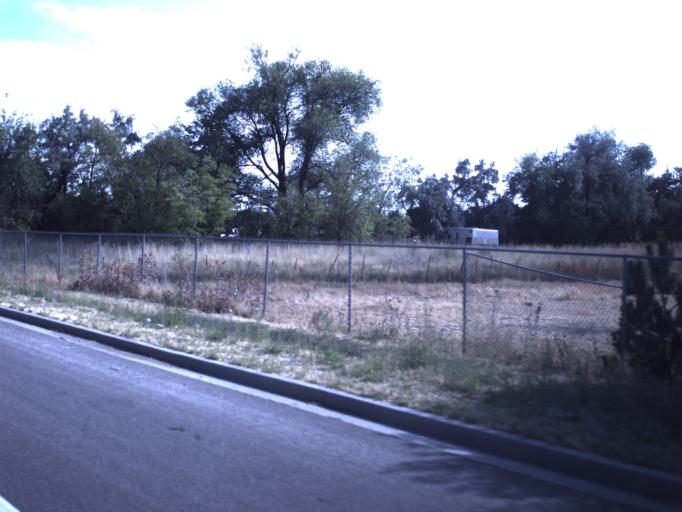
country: US
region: Utah
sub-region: Weber County
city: Harrisville
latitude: 41.2935
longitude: -111.9940
